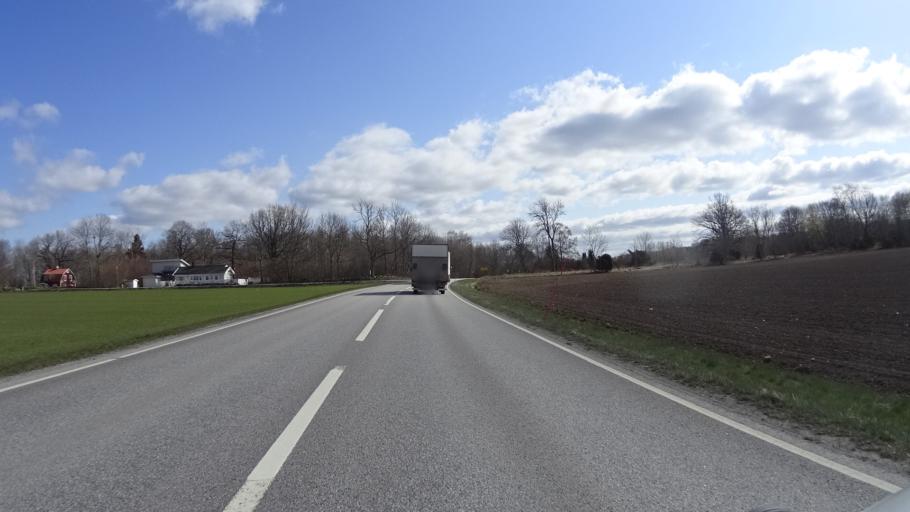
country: SE
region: OEstergoetland
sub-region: Mjolby Kommun
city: Mantorp
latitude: 58.3767
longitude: 15.2718
